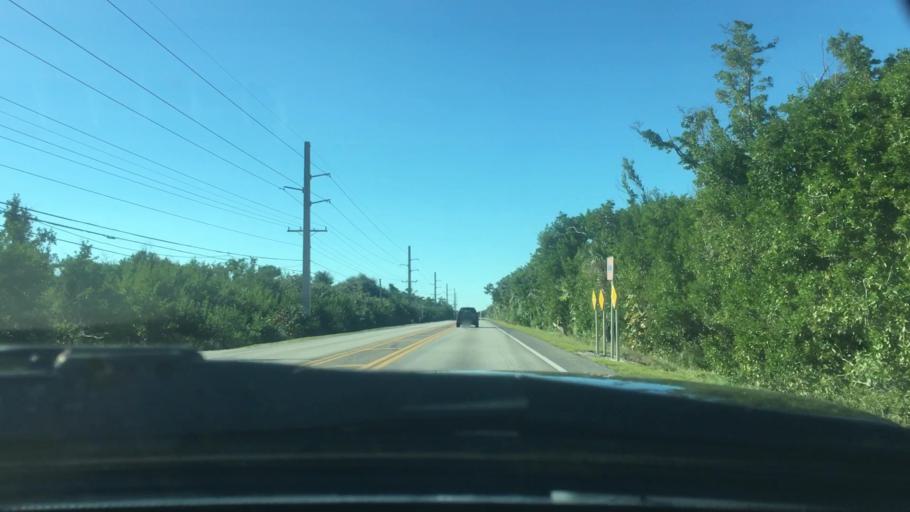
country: US
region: Florida
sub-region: Monroe County
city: Cudjoe Key
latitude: 24.6654
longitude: -81.4917
